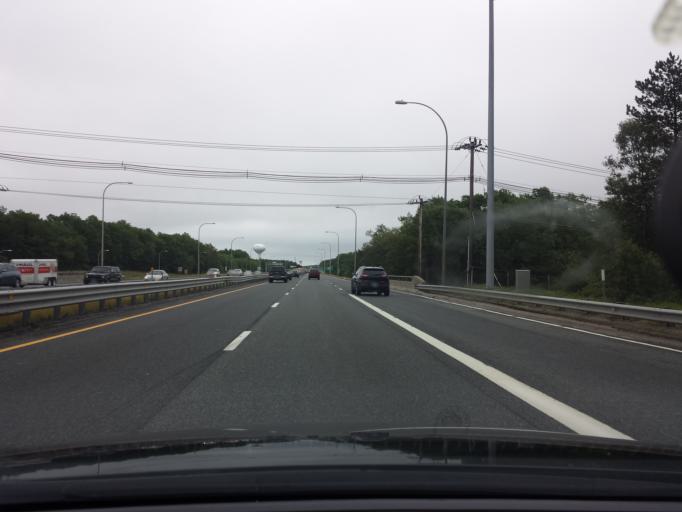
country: US
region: Rhode Island
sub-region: Kent County
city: West Warwick
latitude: 41.6524
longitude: -71.5759
